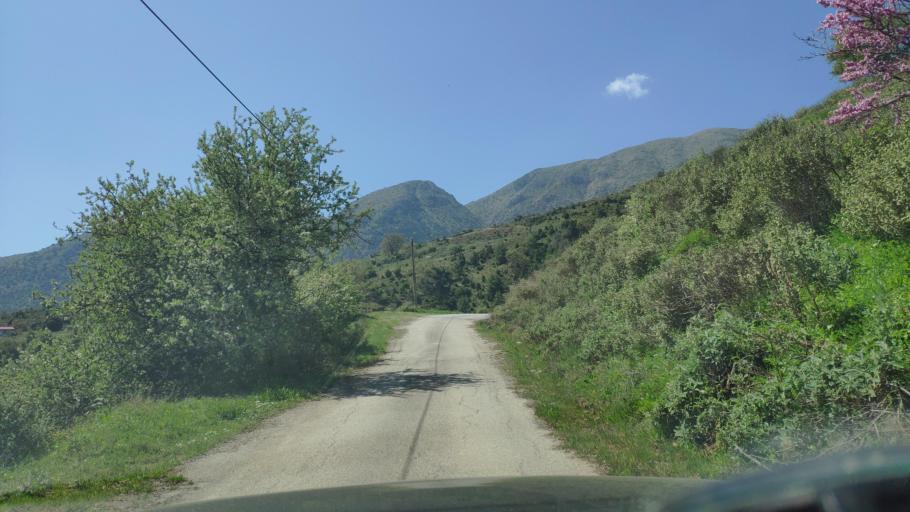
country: GR
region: West Greece
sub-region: Nomos Achaias
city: Akrata
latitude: 38.0836
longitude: 22.3236
